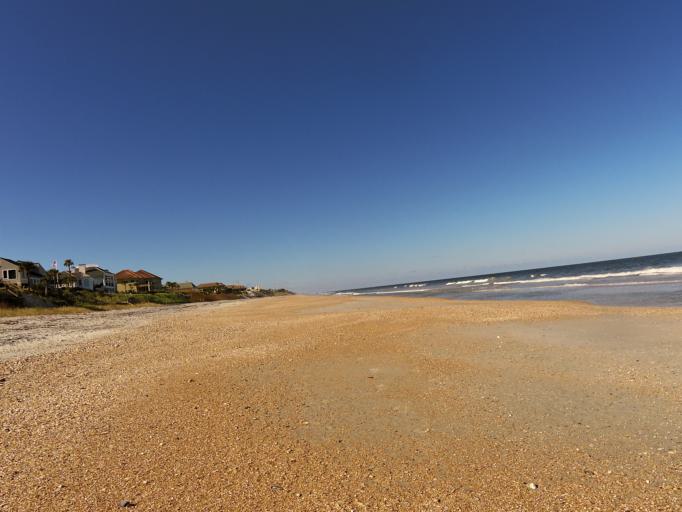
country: US
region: Florida
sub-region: Saint Johns County
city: Sawgrass
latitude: 30.1688
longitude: -81.3576
